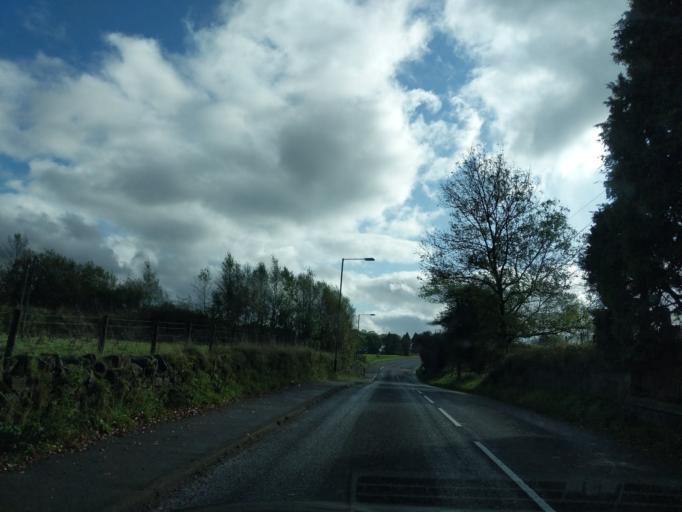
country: GB
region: Scotland
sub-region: Dumfries and Galloway
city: Moffat
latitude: 55.3223
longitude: -3.4460
